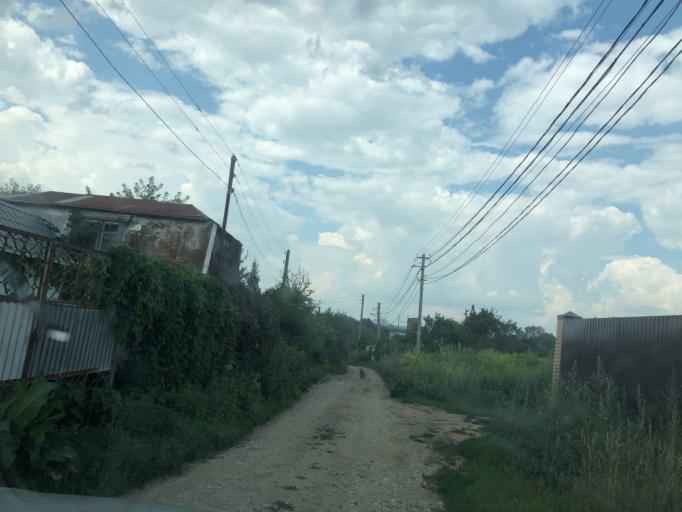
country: RU
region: Tula
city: Mendeleyevskiy
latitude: 54.1592
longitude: 37.5637
